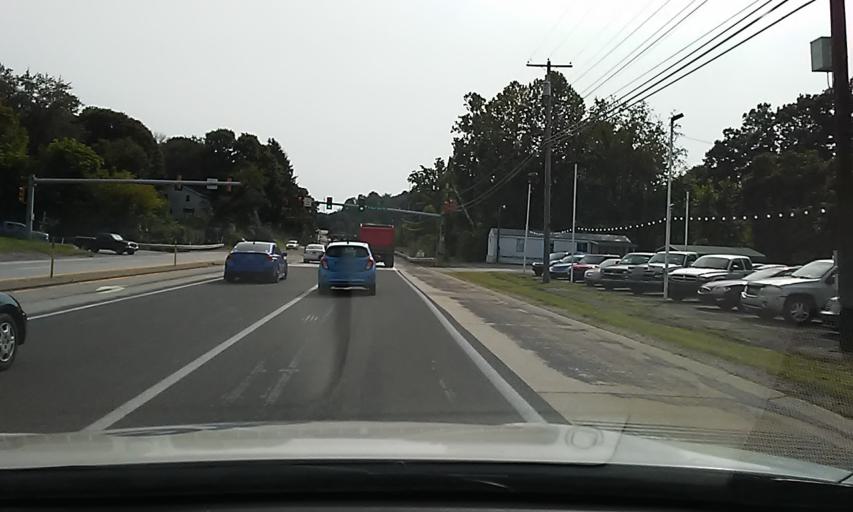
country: US
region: Pennsylvania
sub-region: Fayette County
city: Connellsville
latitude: 40.0449
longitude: -79.5733
